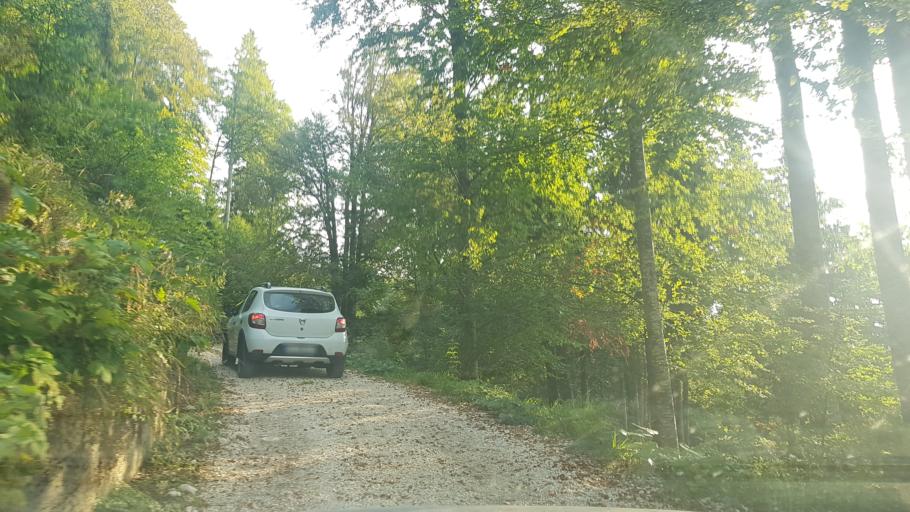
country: SI
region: Bovec
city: Bovec
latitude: 46.4064
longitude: 13.5101
